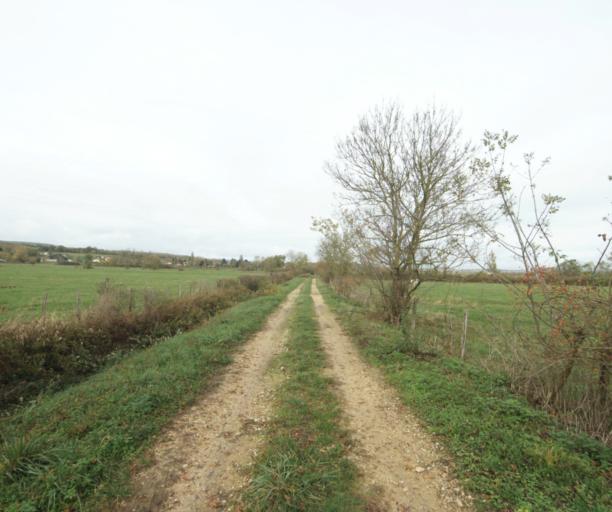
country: FR
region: Rhone-Alpes
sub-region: Departement de l'Ain
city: Pont-de-Vaux
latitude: 46.4516
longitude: 4.8947
